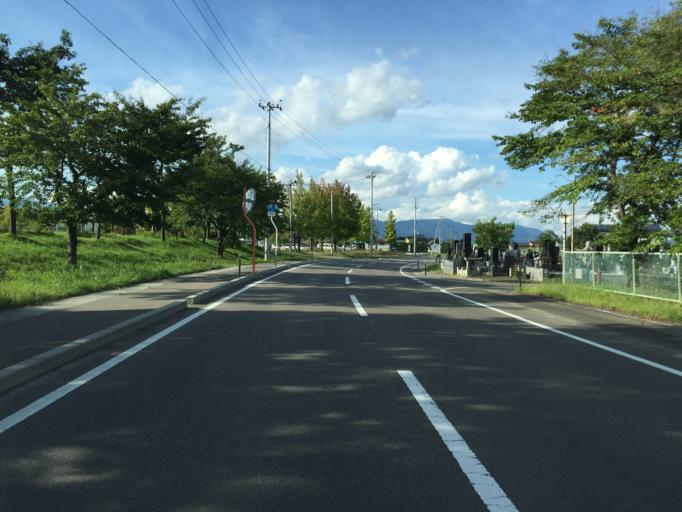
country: JP
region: Fukushima
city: Hobaramachi
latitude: 37.8183
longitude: 140.5717
